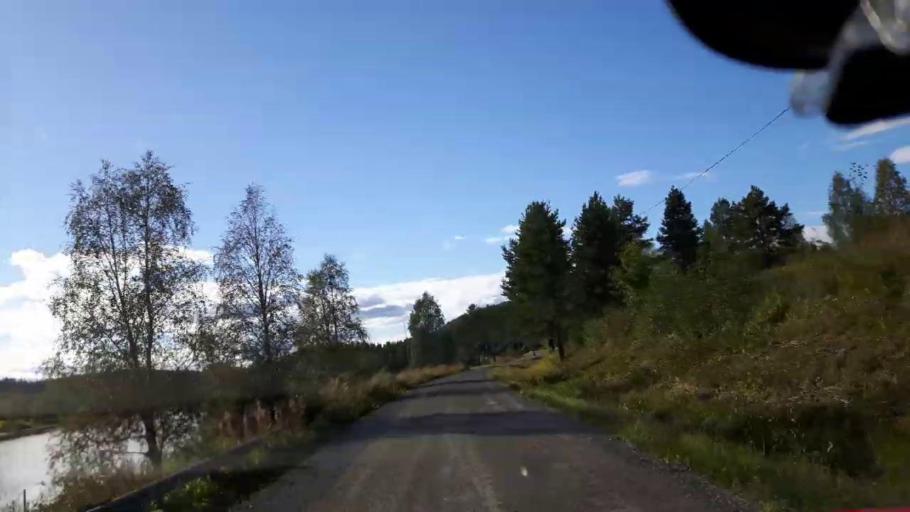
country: SE
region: Jaemtland
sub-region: Ragunda Kommun
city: Hammarstrand
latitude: 63.4863
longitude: 16.0993
